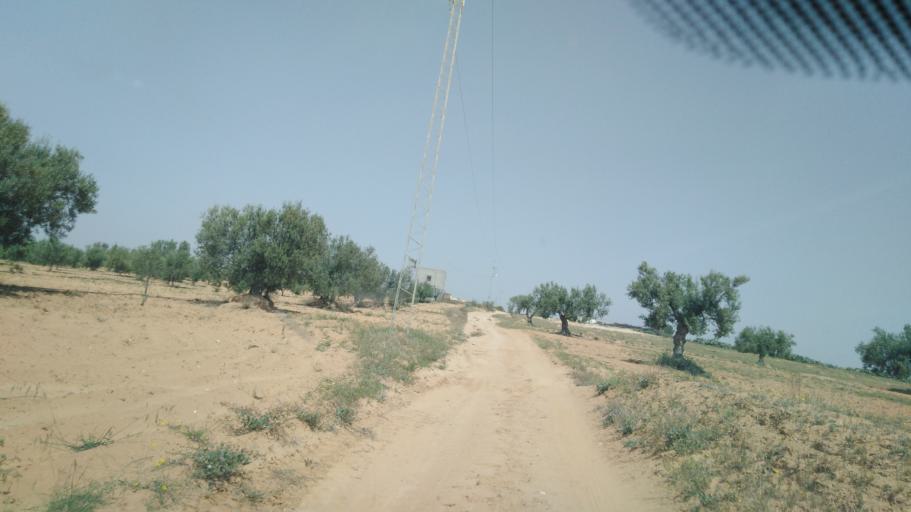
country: TN
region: Safaqis
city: Sfax
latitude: 34.7444
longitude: 10.5698
